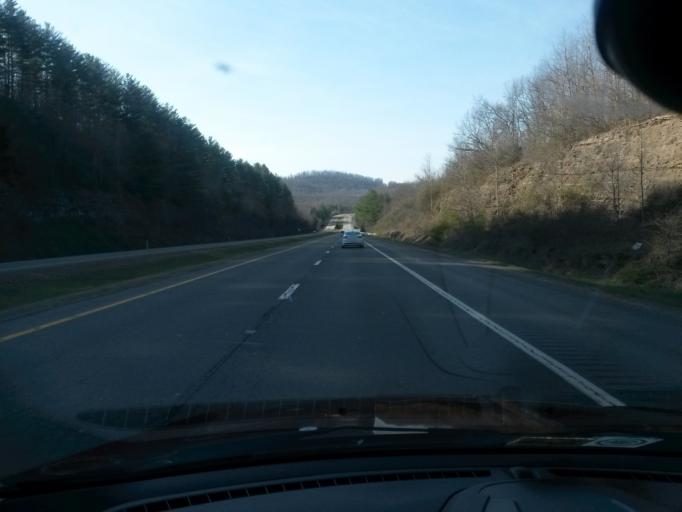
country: US
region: West Virginia
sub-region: Fayette County
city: Oak Hill
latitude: 37.9359
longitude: -81.1584
